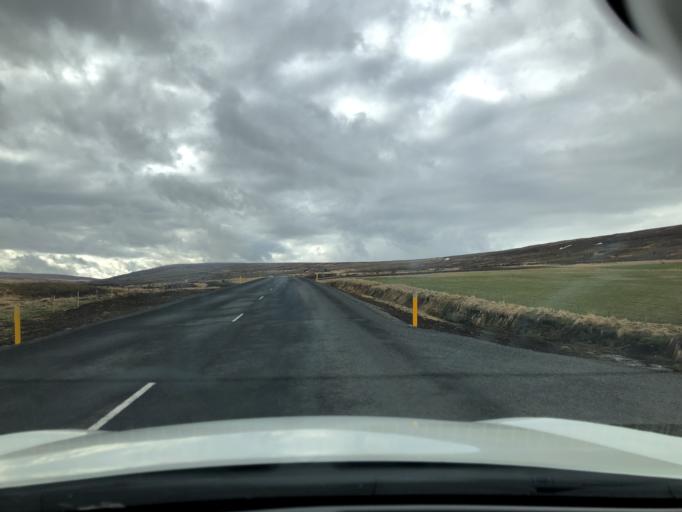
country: IS
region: Northeast
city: Laugar
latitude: 65.6928
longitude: -17.3496
